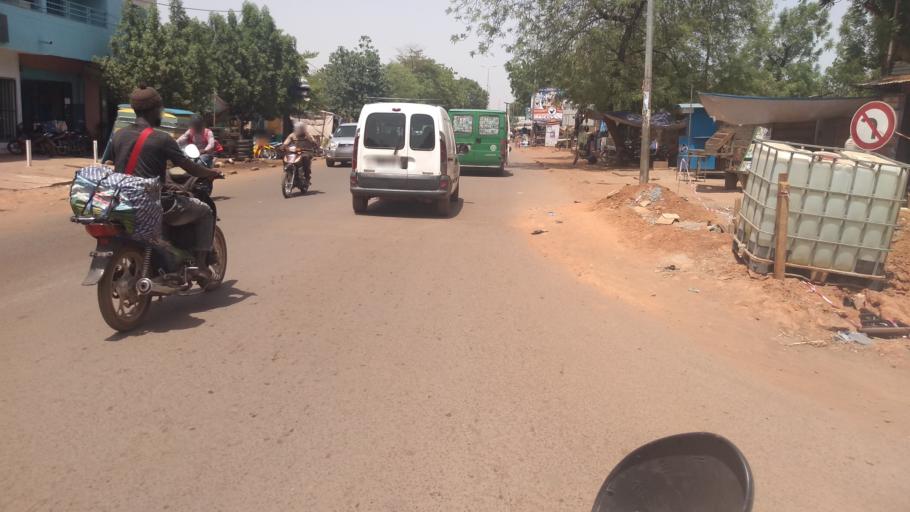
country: ML
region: Bamako
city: Bamako
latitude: 12.6420
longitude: -8.0224
